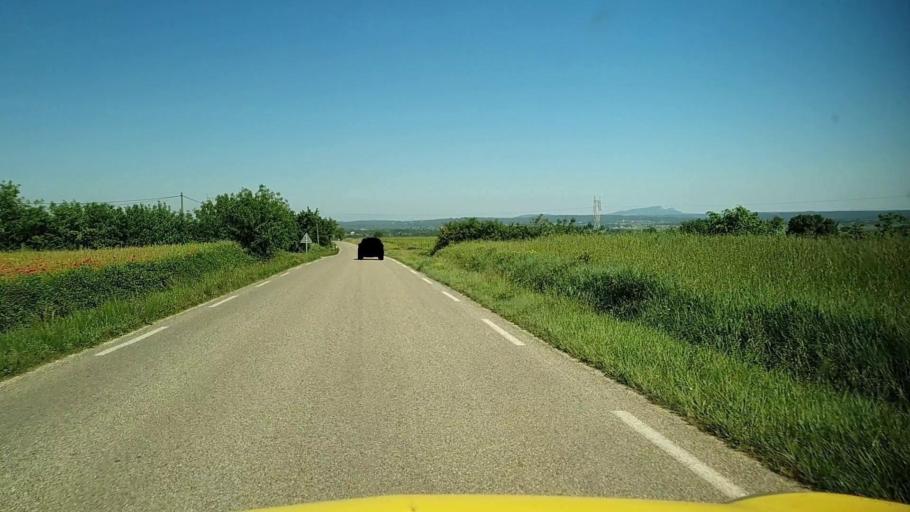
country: FR
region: Languedoc-Roussillon
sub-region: Departement du Gard
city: Blauzac
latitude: 43.9441
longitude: 4.3493
